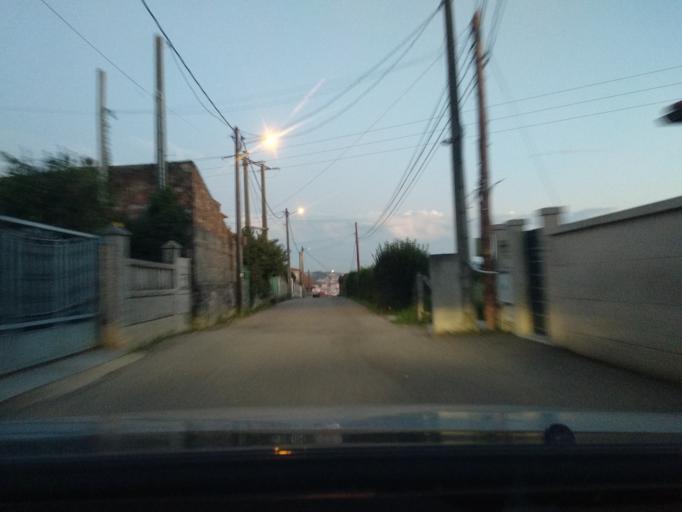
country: ES
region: Galicia
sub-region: Provincia de Pontevedra
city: Moana
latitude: 42.2839
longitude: -8.7480
